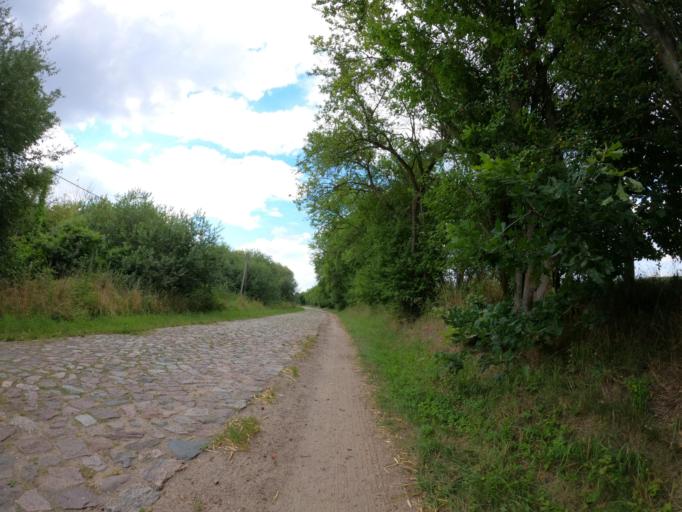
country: DE
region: Mecklenburg-Vorpommern
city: Woldegk
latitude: 53.4112
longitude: 13.6208
